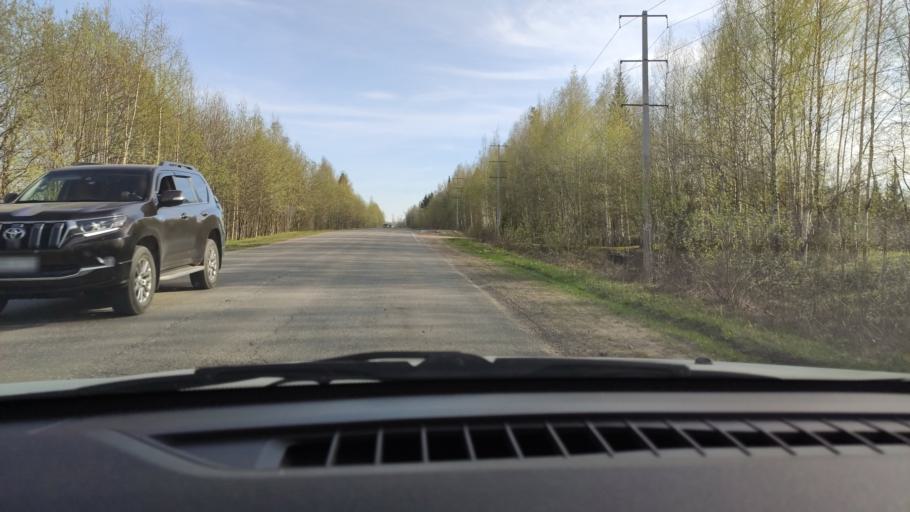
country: RU
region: Perm
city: Novyye Lyady
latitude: 57.9494
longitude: 56.5687
